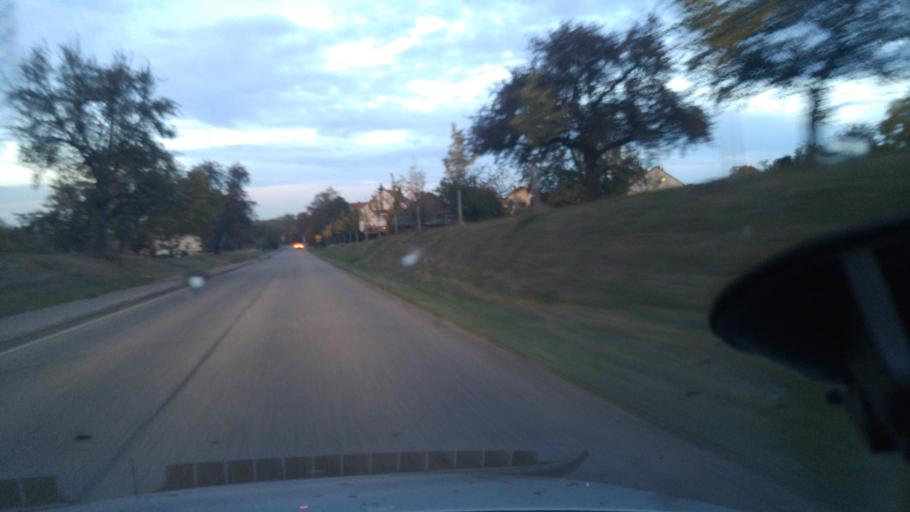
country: DE
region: Baden-Wuerttemberg
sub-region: Regierungsbezirk Stuttgart
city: Ditzingen
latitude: 48.8206
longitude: 9.0591
